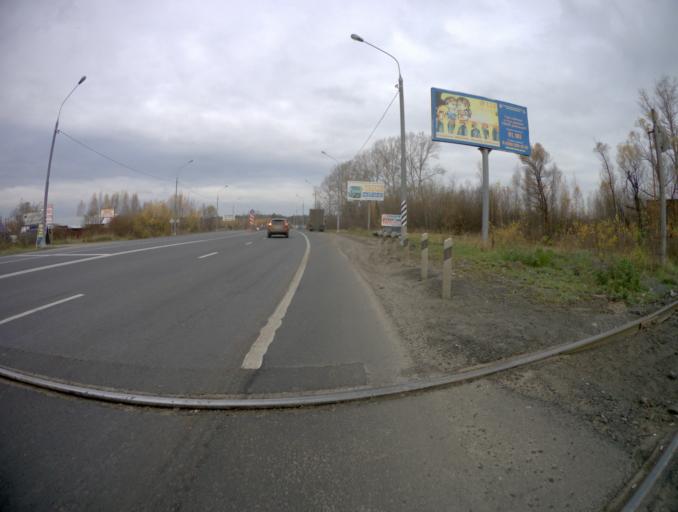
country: RU
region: Moskovskaya
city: Orekhovo-Zuyevo
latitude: 55.8408
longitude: 38.9695
